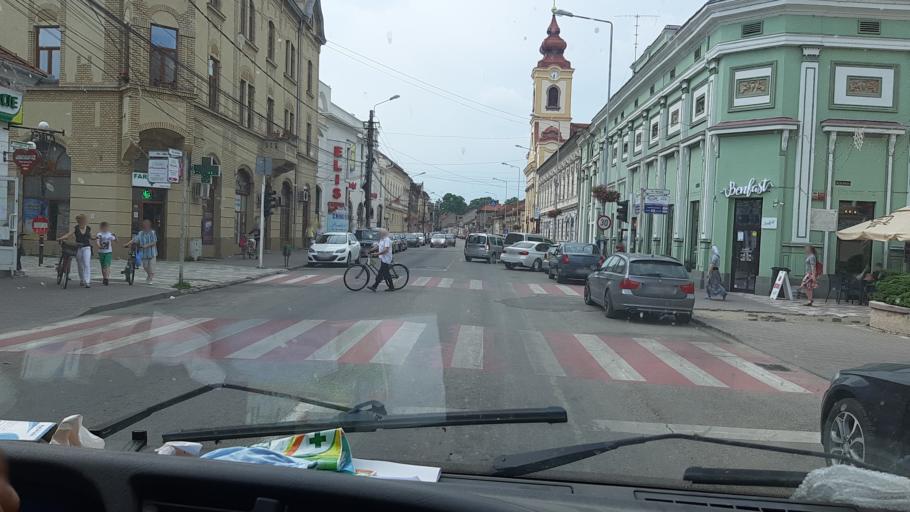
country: RO
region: Timis
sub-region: Municipiul Lugoj
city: Lugoj
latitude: 45.6827
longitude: 21.9021
